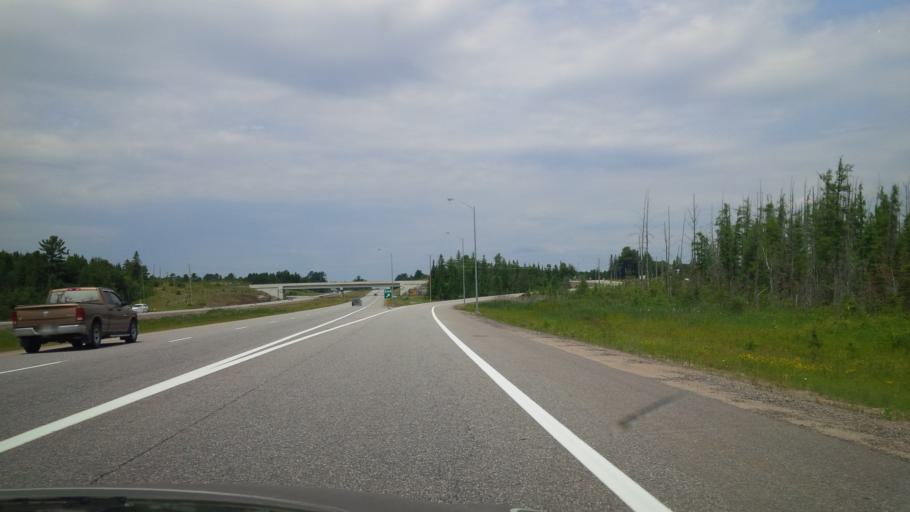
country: CA
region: Ontario
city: Huntsville
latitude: 45.5080
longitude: -79.3028
